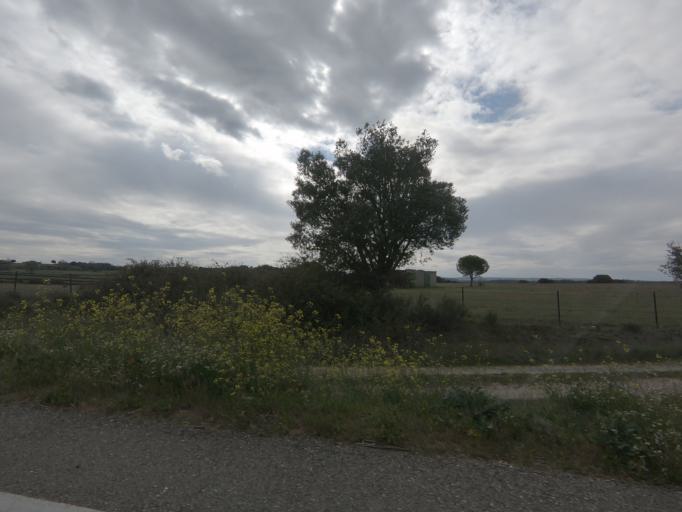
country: ES
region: Castille and Leon
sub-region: Provincia de Salamanca
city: Robleda
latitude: 40.3959
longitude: -6.6068
